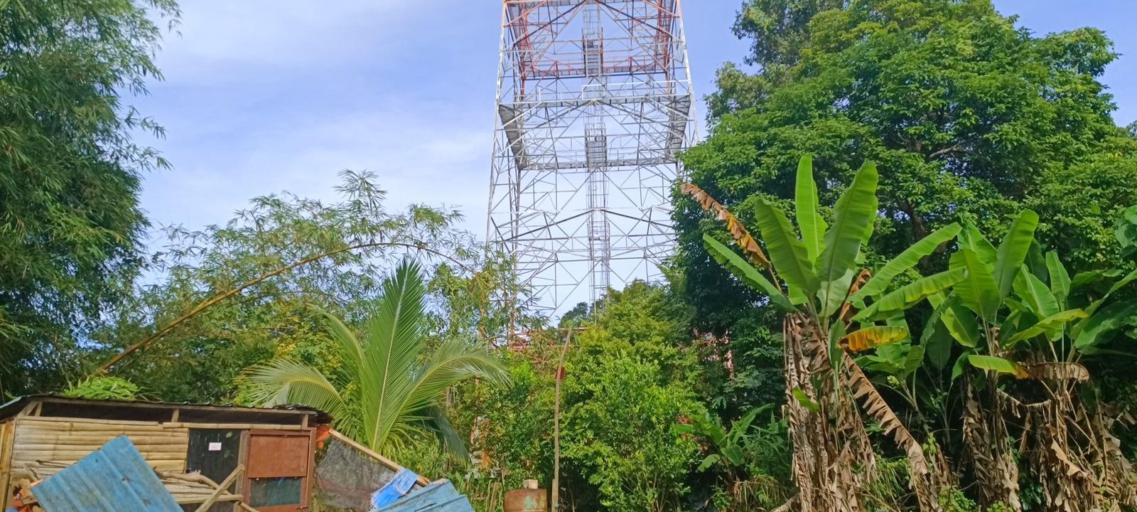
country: MY
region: Penang
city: Kampung Sungai Ara
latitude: 5.3794
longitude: 100.2608
